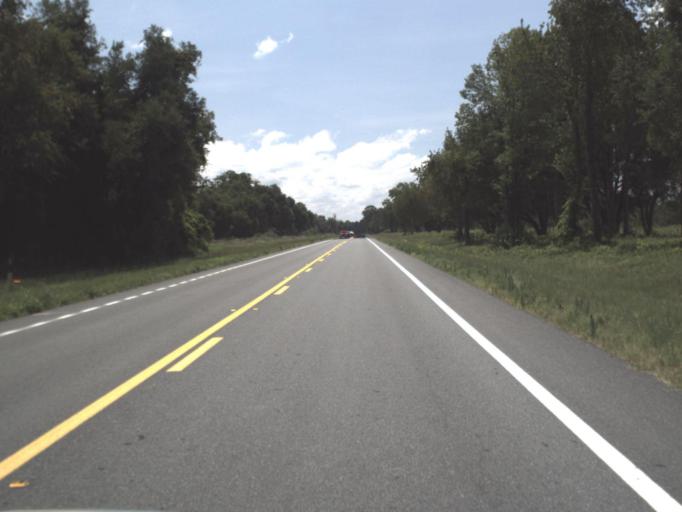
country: US
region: Florida
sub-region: Hamilton County
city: Jasper
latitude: 30.3993
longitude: -82.8343
